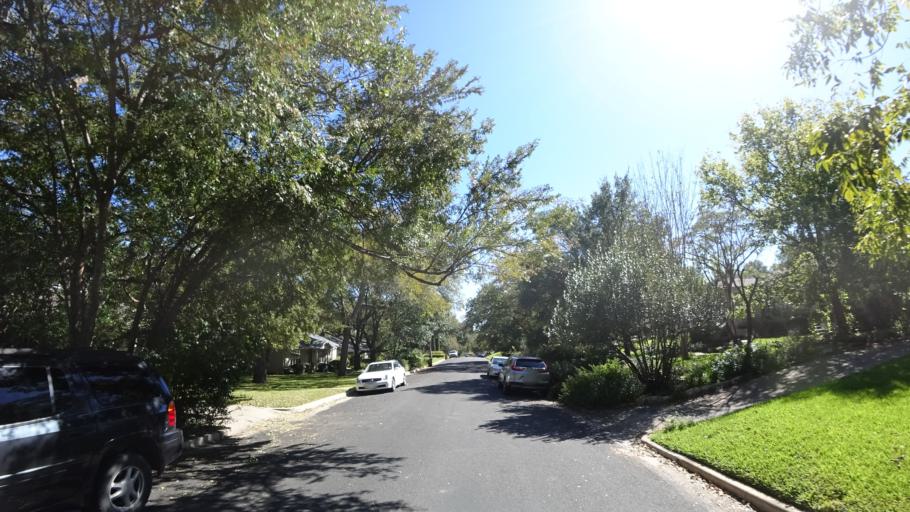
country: US
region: Texas
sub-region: Travis County
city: Rollingwood
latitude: 30.2980
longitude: -97.7635
